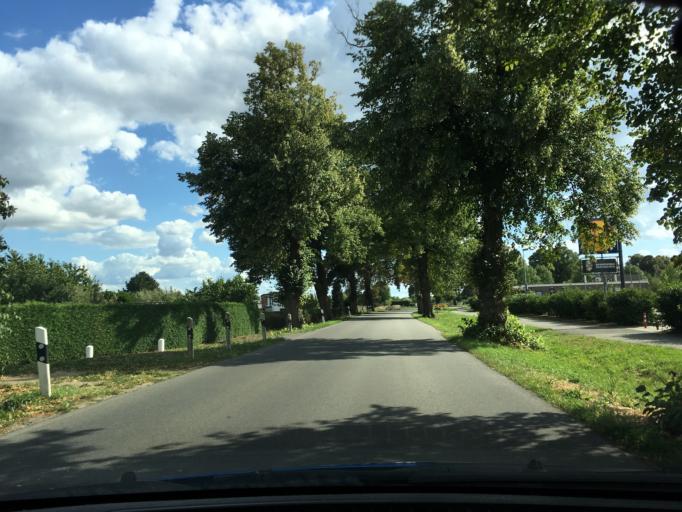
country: DE
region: Mecklenburg-Vorpommern
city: Boizenburg
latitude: 53.3873
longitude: 10.7355
